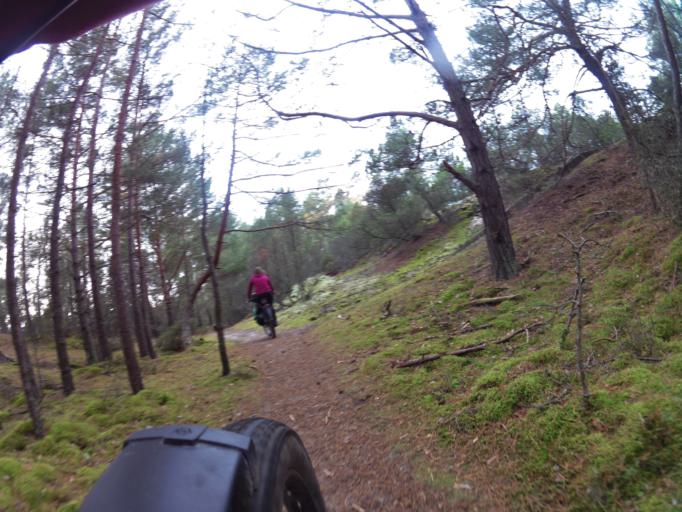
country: PL
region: Pomeranian Voivodeship
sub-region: Powiat pucki
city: Hel
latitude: 54.6190
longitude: 18.8218
